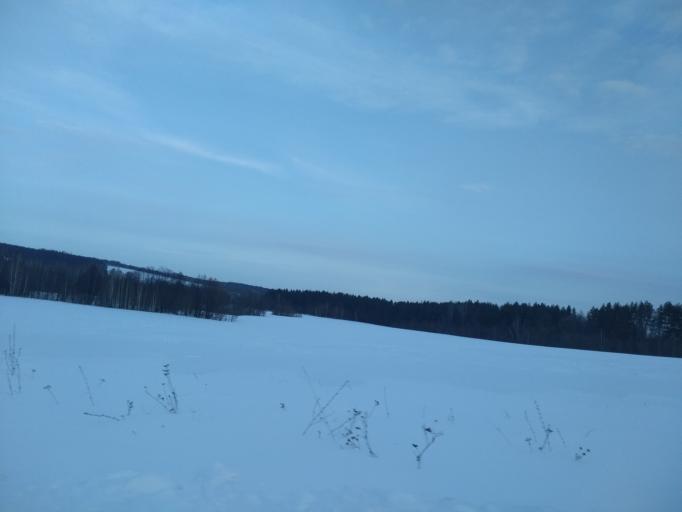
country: RU
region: Bashkortostan
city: Kudeyevskiy
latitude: 54.7156
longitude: 56.6312
